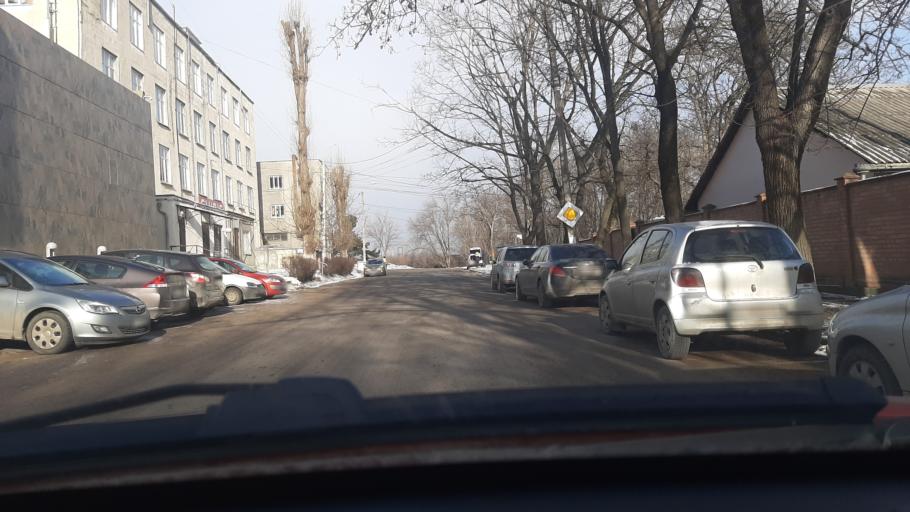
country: MD
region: Chisinau
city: Chisinau
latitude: 47.0044
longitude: 28.8130
